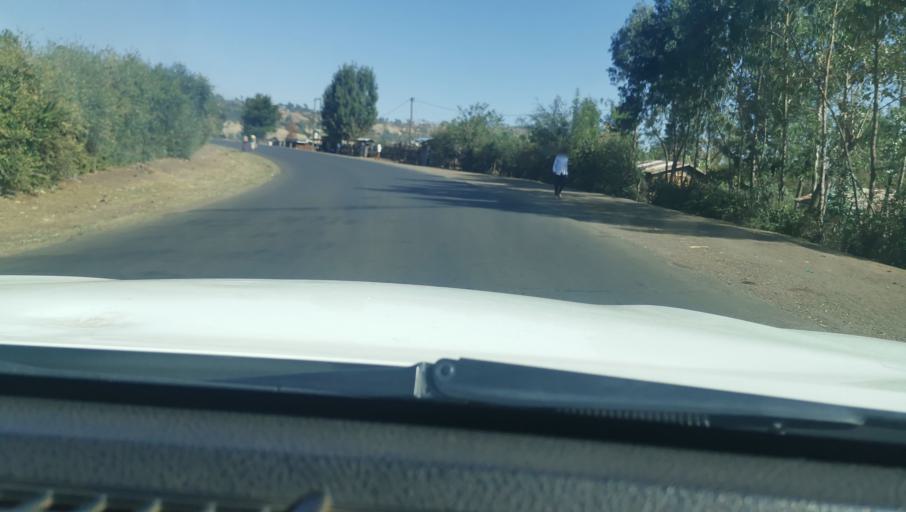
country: ET
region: Oromiya
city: Gedo
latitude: 8.9676
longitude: 37.5224
